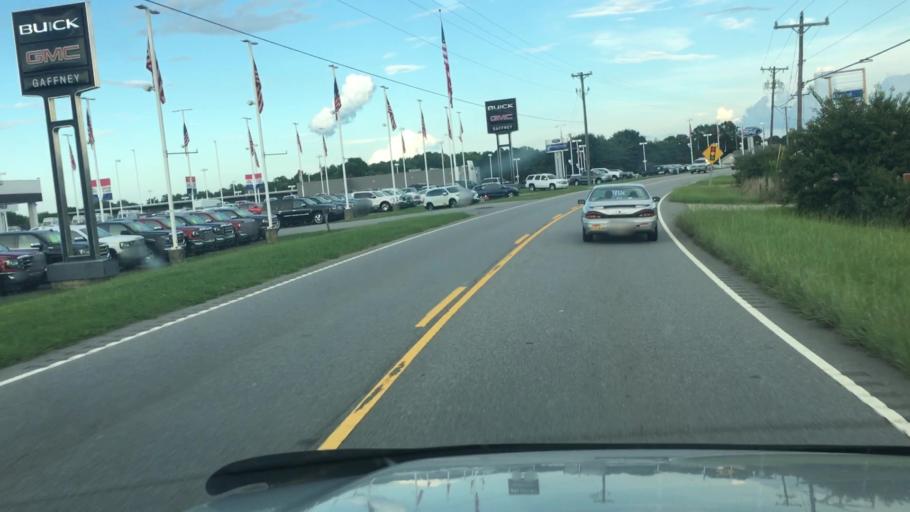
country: US
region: South Carolina
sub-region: Cherokee County
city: Gaffney
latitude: 35.1042
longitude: -81.6836
